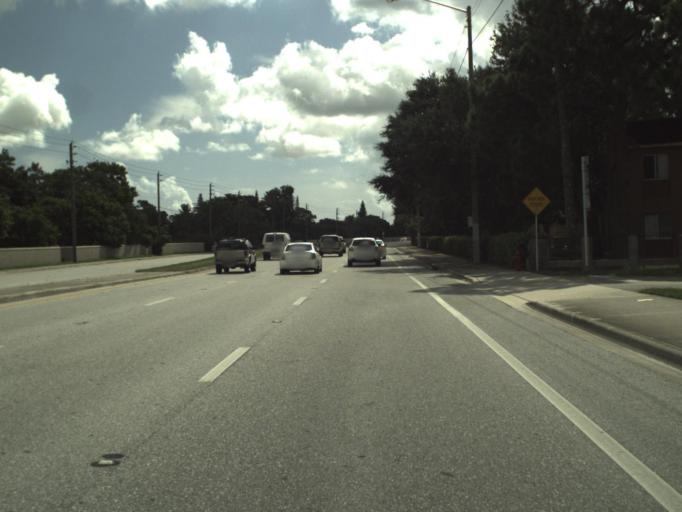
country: US
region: Florida
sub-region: Palm Beach County
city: Greenacres City
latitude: 26.6515
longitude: -80.1415
